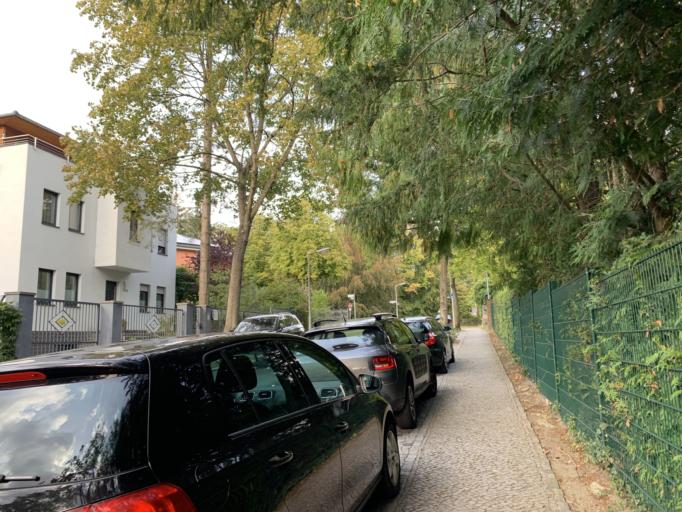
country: DE
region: Berlin
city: Wannsee
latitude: 52.4182
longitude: 13.1624
